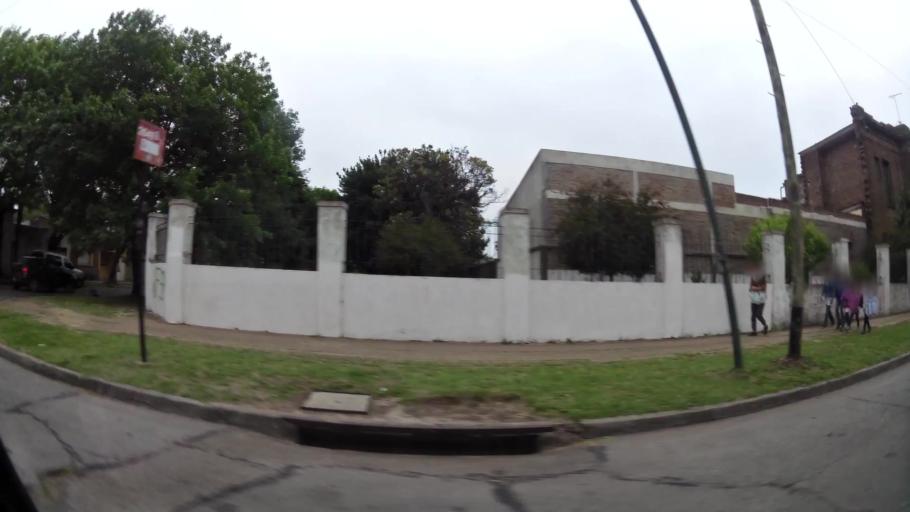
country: AR
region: Buenos Aires
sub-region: Partido de La Plata
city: La Plata
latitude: -34.9205
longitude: -57.9785
